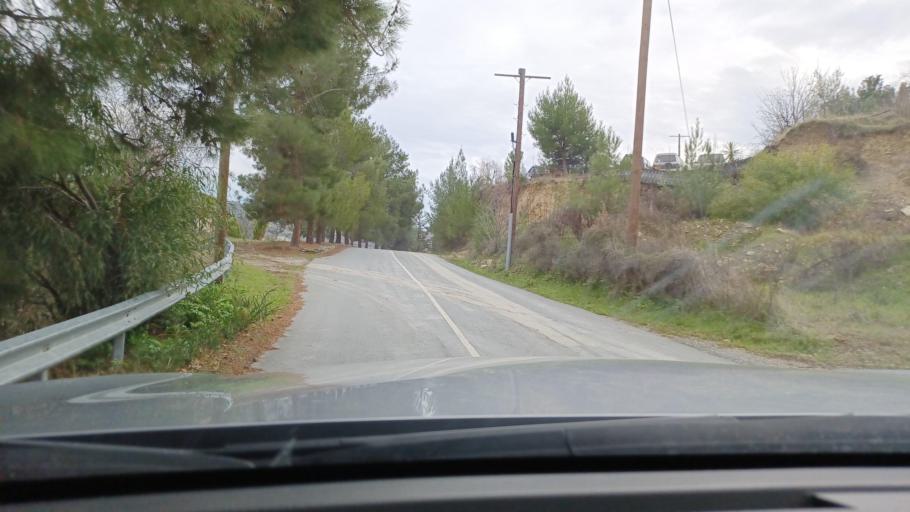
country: CY
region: Limassol
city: Pelendri
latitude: 34.8179
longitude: 32.8972
